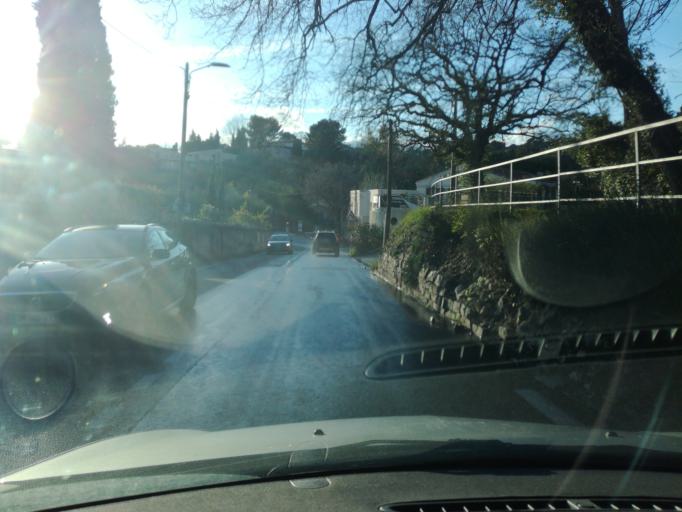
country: FR
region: Provence-Alpes-Cote d'Azur
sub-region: Departement des Alpes-Maritimes
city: Mougins
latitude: 43.6045
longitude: 7.0030
